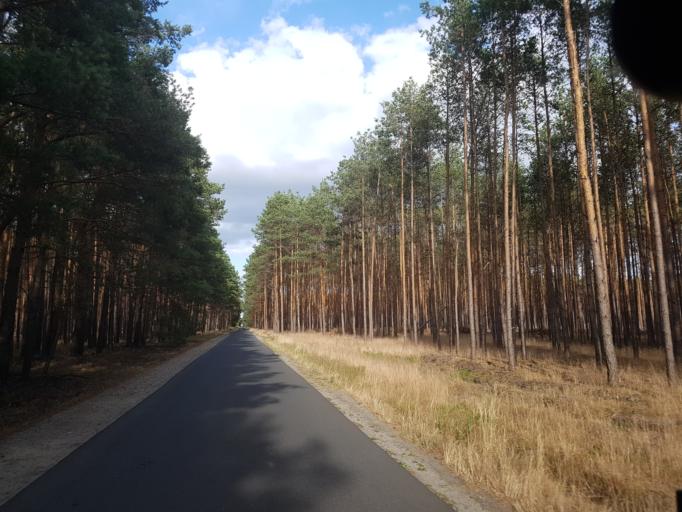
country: DE
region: Brandenburg
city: Herzberg
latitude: 51.7593
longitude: 13.2344
